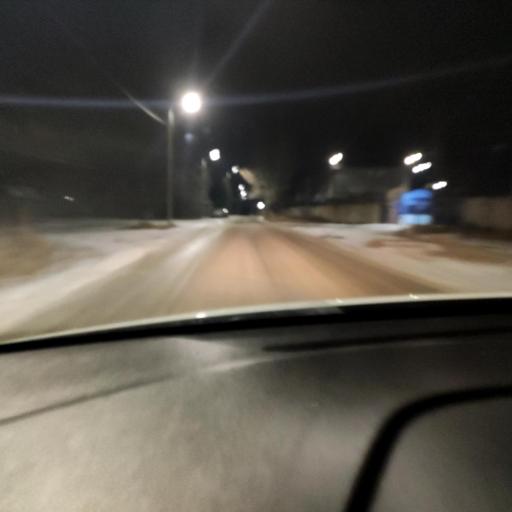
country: RU
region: Tatarstan
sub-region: Gorod Kazan'
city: Kazan
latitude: 55.7241
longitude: 49.0997
